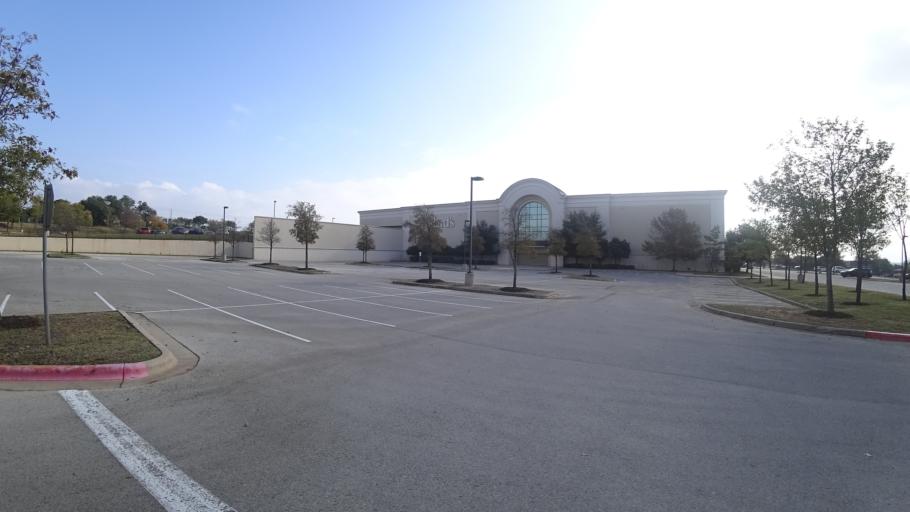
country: US
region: Texas
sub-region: Travis County
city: Bee Cave
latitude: 30.3105
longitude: -97.9450
